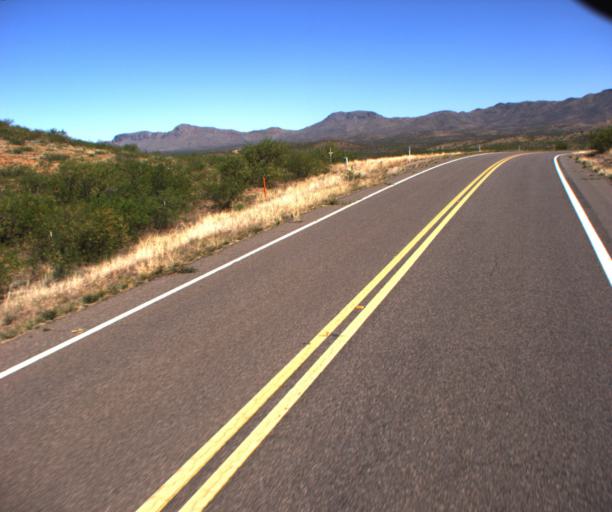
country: US
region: Arizona
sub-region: Cochise County
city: Douglas
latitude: 31.4845
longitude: -109.4405
